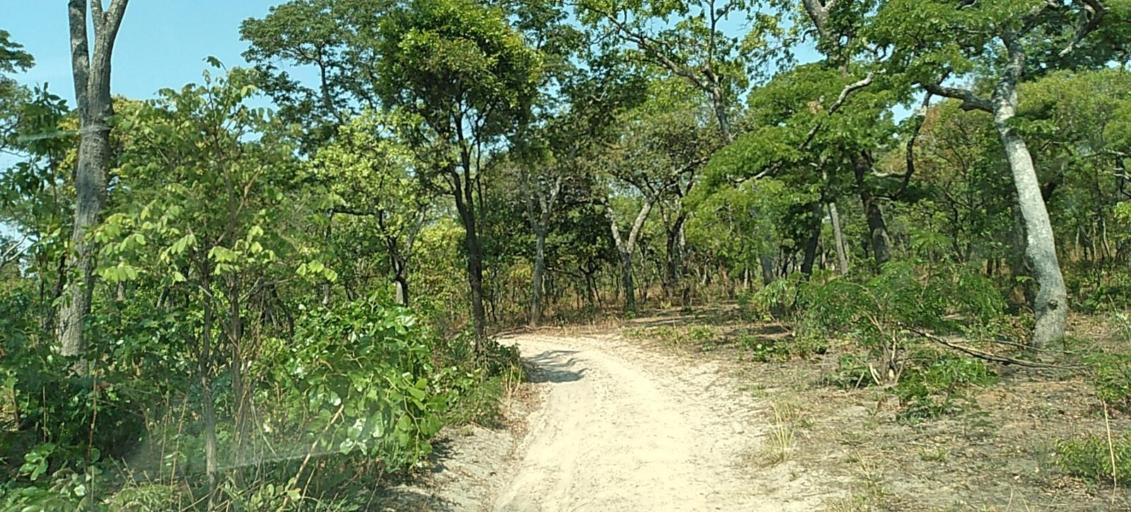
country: ZM
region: Copperbelt
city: Mpongwe
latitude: -13.7907
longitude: 28.0930
